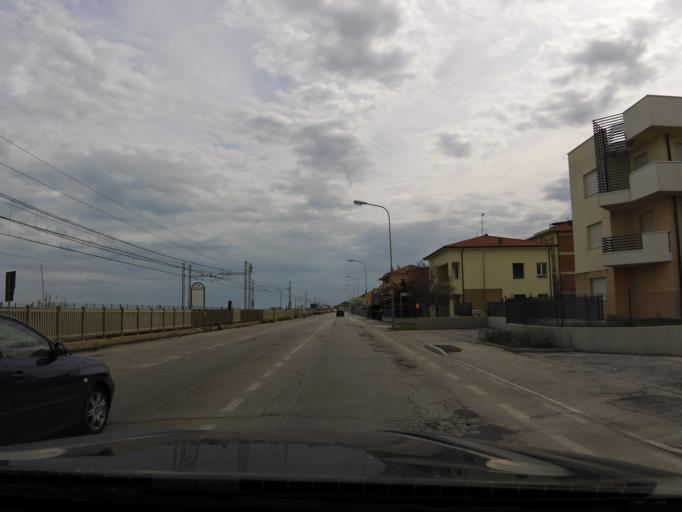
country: IT
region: The Marches
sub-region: Provincia di Macerata
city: Porto Potenza Picena
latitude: 43.3364
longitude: 13.7096
